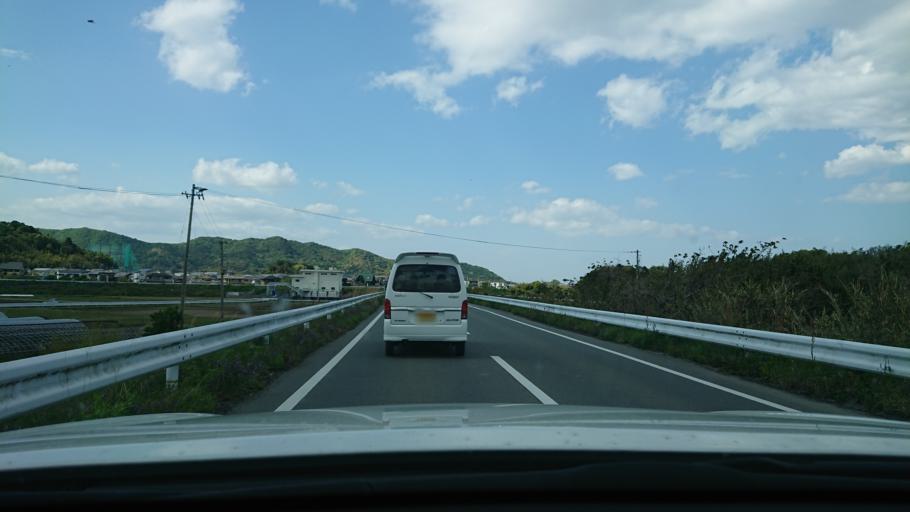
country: JP
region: Tokushima
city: Komatsushimacho
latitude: 33.9972
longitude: 134.5477
